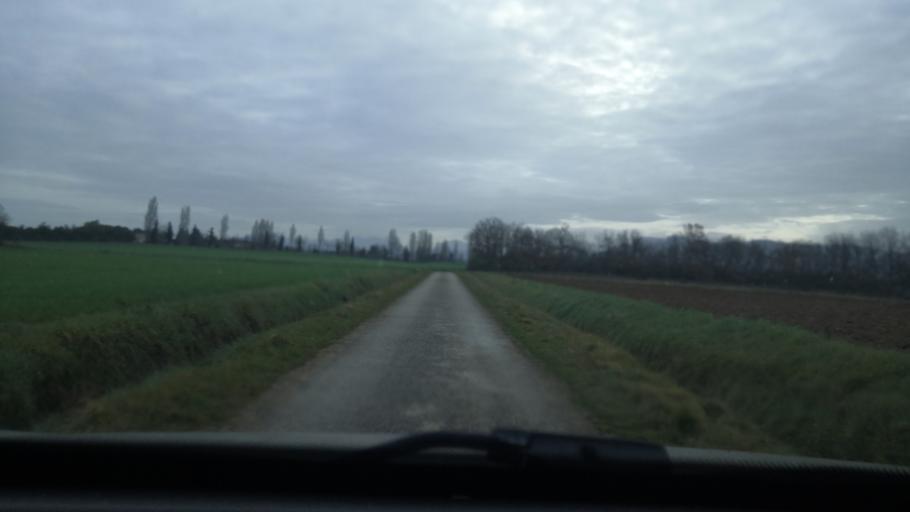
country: FR
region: Rhone-Alpes
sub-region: Departement de la Drome
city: La Begude-de-Mazenc
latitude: 44.5647
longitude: 4.8857
